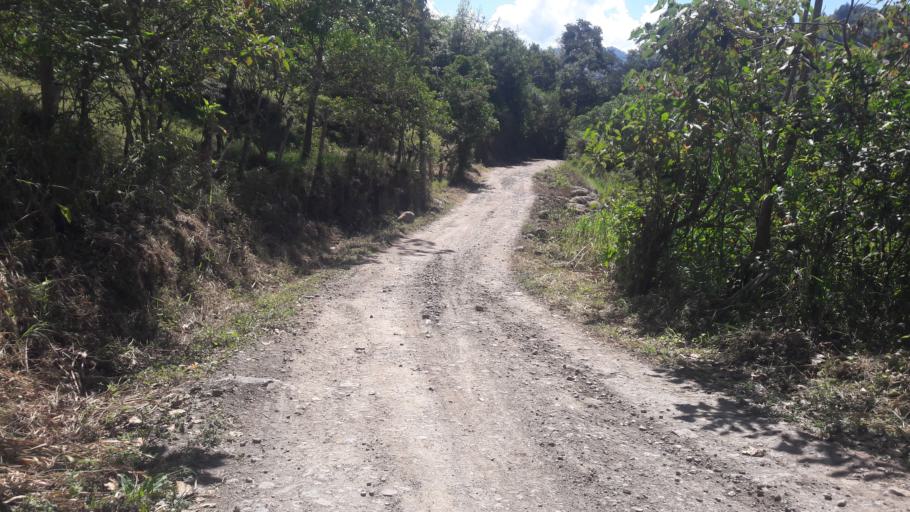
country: CO
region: Cundinamarca
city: Tenza
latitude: 5.0810
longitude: -73.4184
